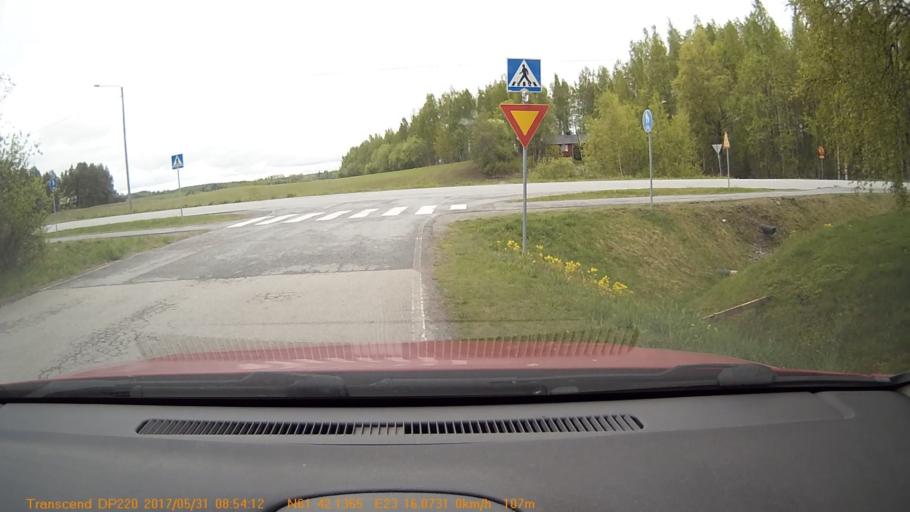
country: FI
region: Pirkanmaa
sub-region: Tampere
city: Viljakkala
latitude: 61.7023
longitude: 23.2679
